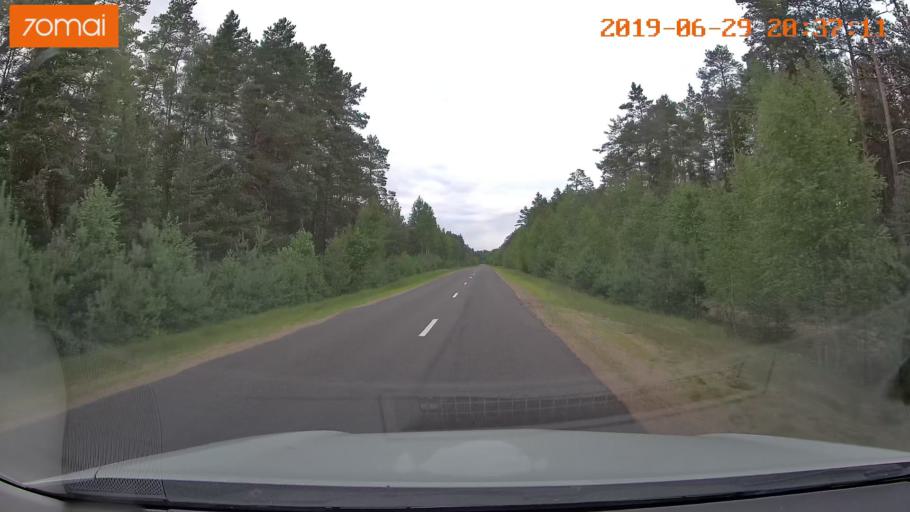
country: BY
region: Brest
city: Hantsavichy
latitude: 52.5349
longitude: 26.3635
